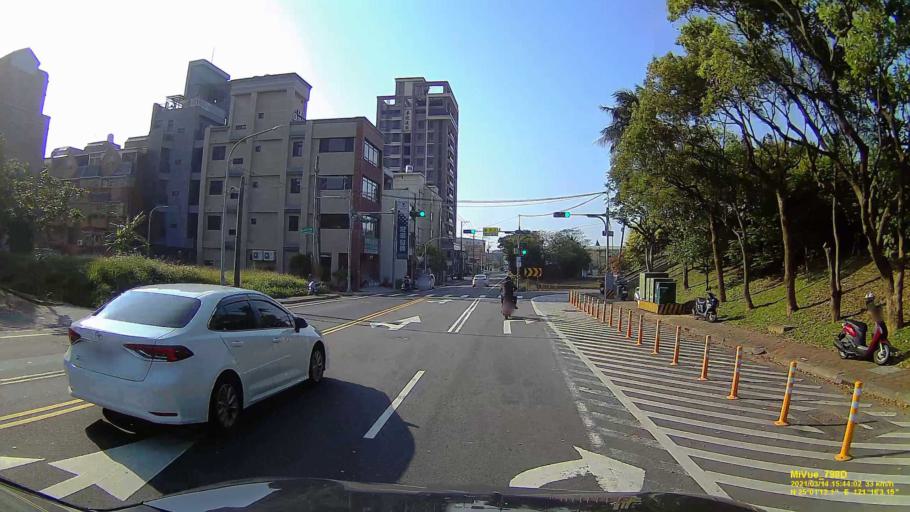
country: TW
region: Taiwan
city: Taoyuan City
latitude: 25.0202
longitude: 121.2673
